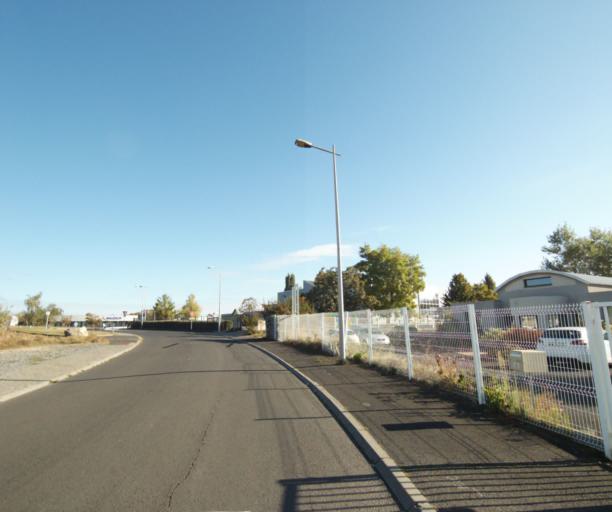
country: FR
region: Auvergne
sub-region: Departement du Puy-de-Dome
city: Cebazat
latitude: 45.8370
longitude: 3.1180
